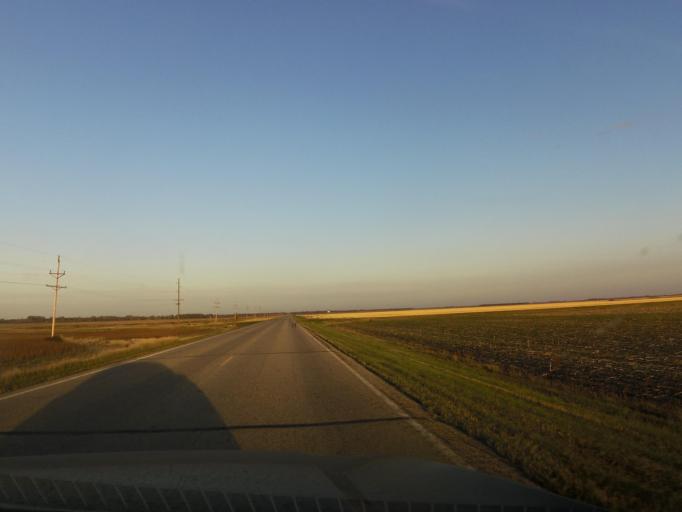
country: CA
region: Manitoba
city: Altona
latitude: 48.9637
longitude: -97.4934
